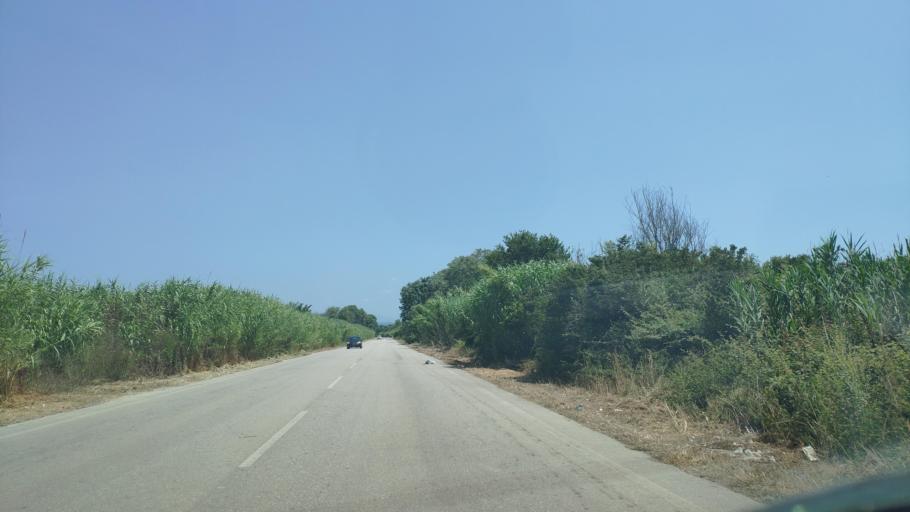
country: GR
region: Epirus
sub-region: Nomos Artas
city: Aneza
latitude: 39.0931
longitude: 20.9035
